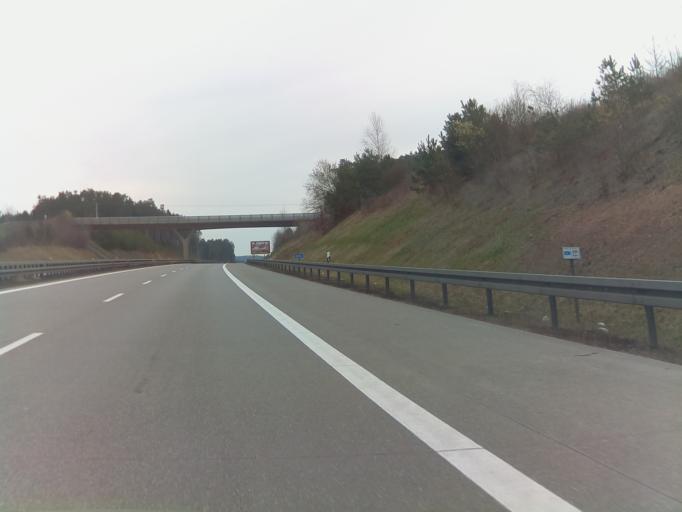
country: DE
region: Bavaria
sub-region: Upper Palatinate
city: Freudenberg
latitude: 49.4290
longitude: 12.0118
